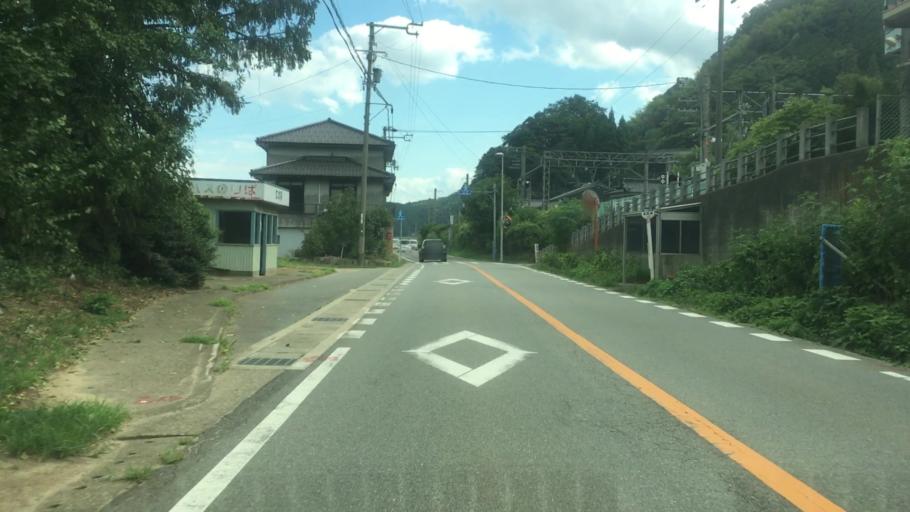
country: JP
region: Hyogo
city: Toyooka
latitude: 35.5887
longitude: 134.7994
